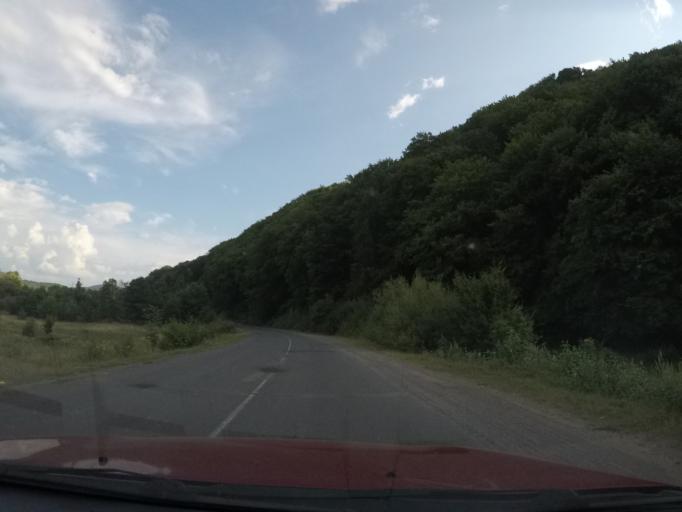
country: UA
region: Zakarpattia
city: Velykyi Bereznyi
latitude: 48.9219
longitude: 22.4554
